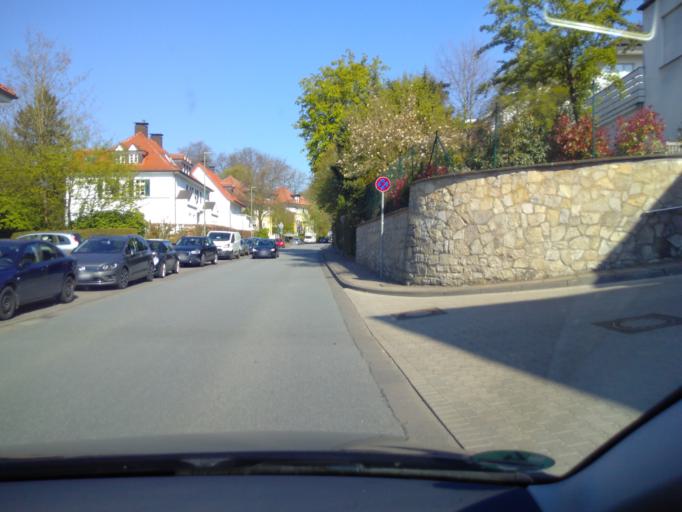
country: DE
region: North Rhine-Westphalia
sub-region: Regierungsbezirk Detmold
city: Bielefeld
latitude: 52.0165
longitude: 8.5171
